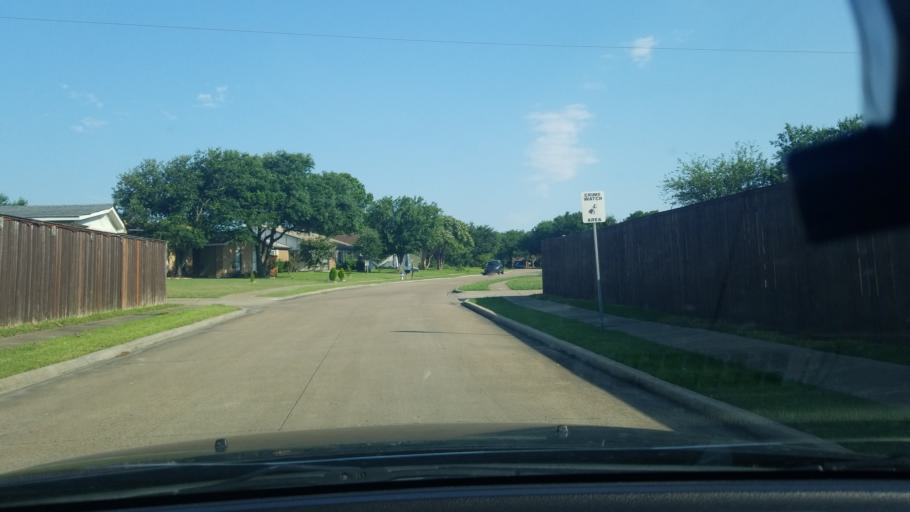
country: US
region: Texas
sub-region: Dallas County
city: Mesquite
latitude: 32.8304
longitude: -96.6334
